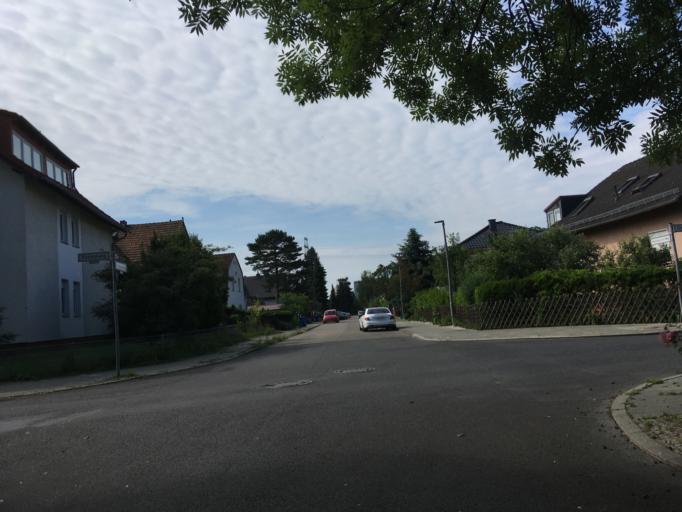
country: DE
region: Berlin
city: Biesdorf
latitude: 52.5178
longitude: 13.5331
